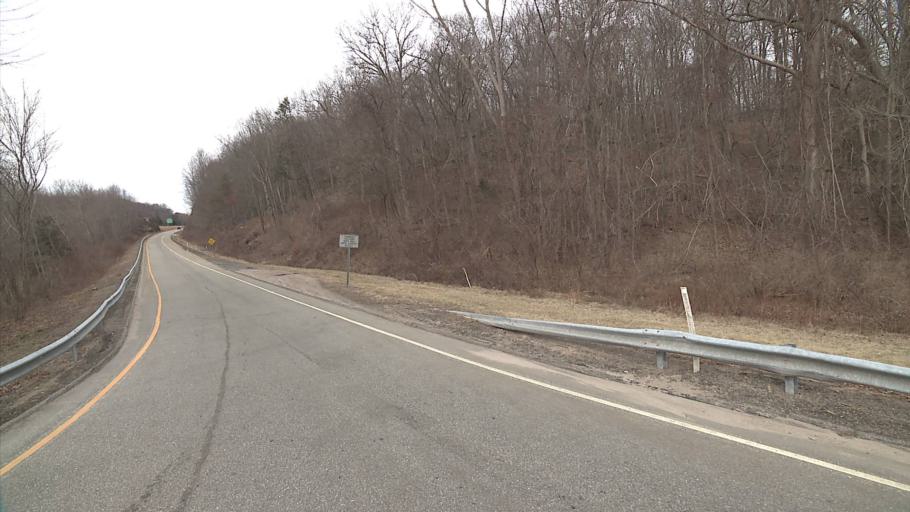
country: US
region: Connecticut
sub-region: Middlesex County
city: Chester Center
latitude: 41.4000
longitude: -72.4718
